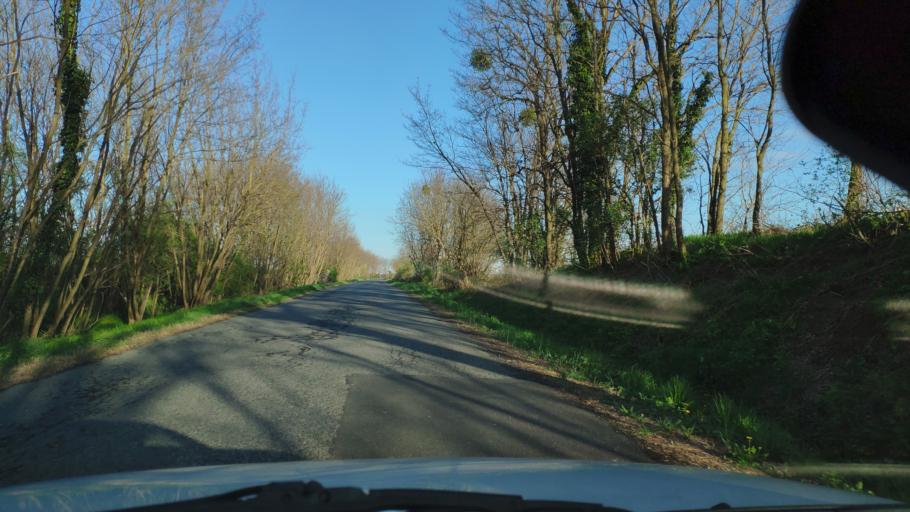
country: HU
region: Zala
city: Zalakomar
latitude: 46.4381
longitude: 17.1297
